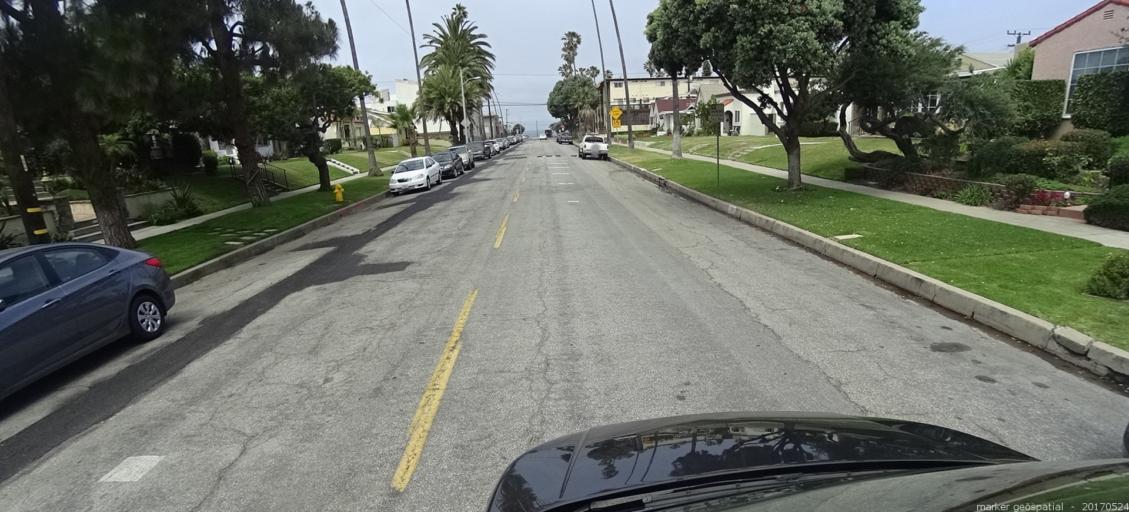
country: US
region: California
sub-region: Los Angeles County
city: Palos Verdes Estates
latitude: 33.8225
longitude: -118.3867
